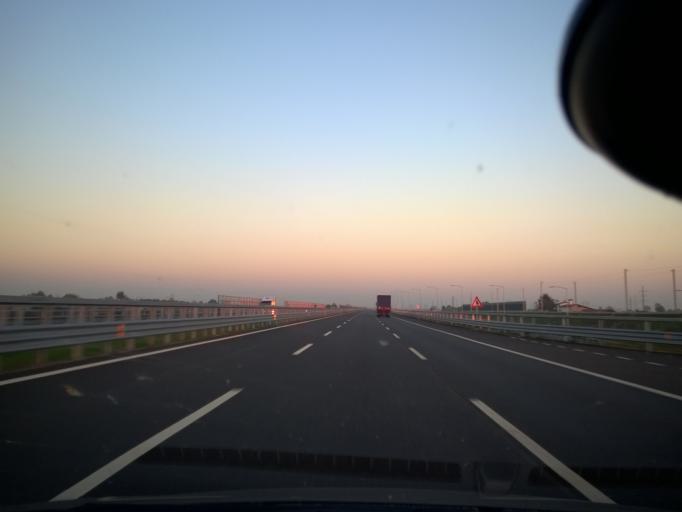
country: IT
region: Lombardy
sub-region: Provincia di Brescia
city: Castelcovati
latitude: 45.5193
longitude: 9.9384
